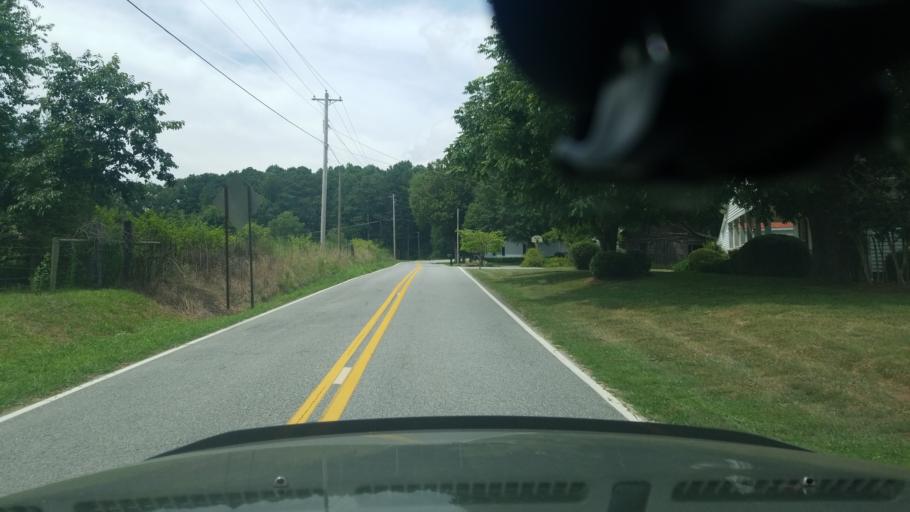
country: US
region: Georgia
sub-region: Forsyth County
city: Cumming
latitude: 34.2242
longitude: -84.2122
